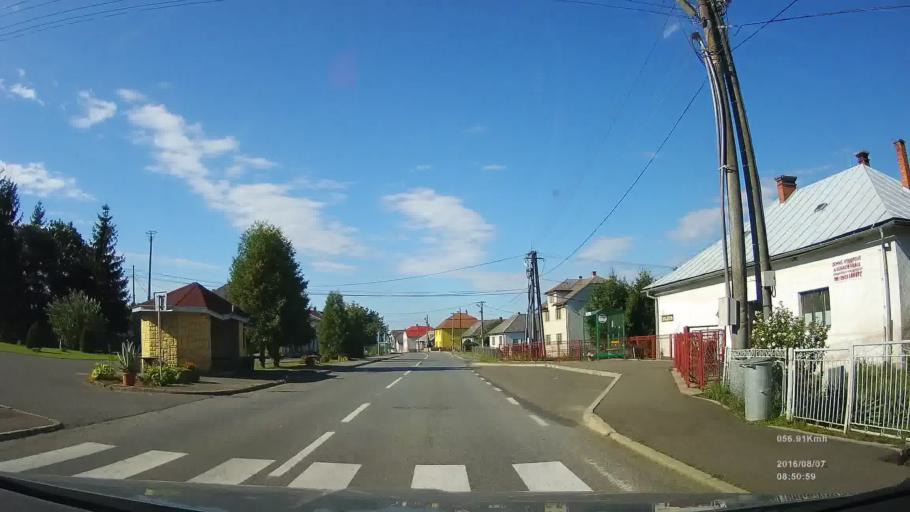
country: SK
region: Presovsky
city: Stropkov
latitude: 49.2419
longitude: 21.6782
